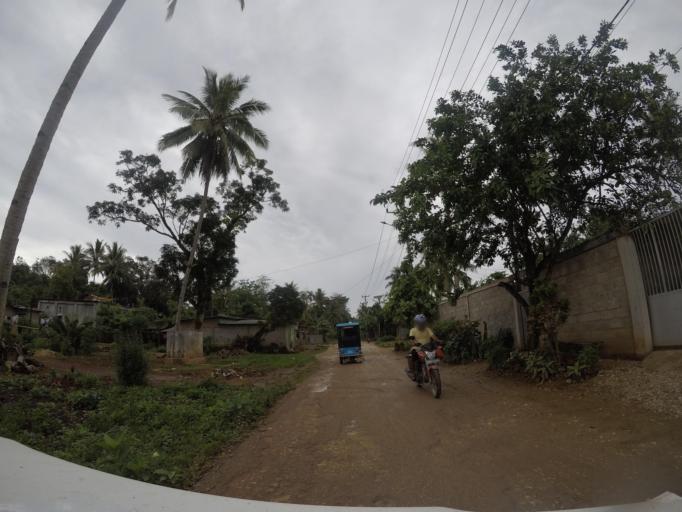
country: TL
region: Lautem
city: Lospalos
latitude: -8.5286
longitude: 126.9981
